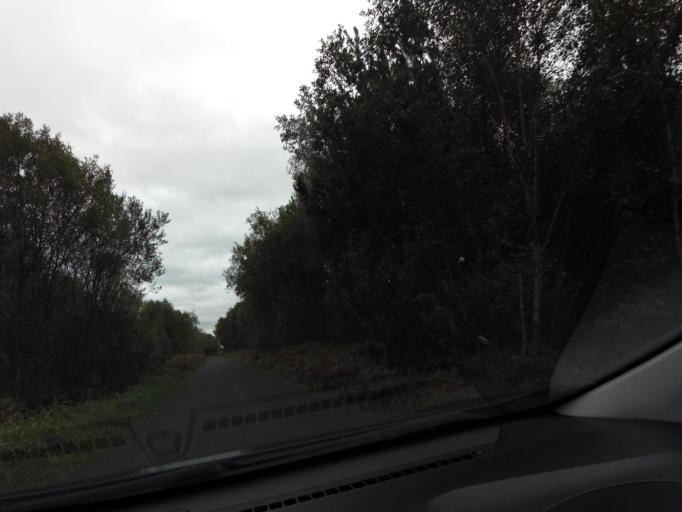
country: IE
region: Leinster
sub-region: Uibh Fhaili
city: Ferbane
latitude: 53.2030
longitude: -7.7247
